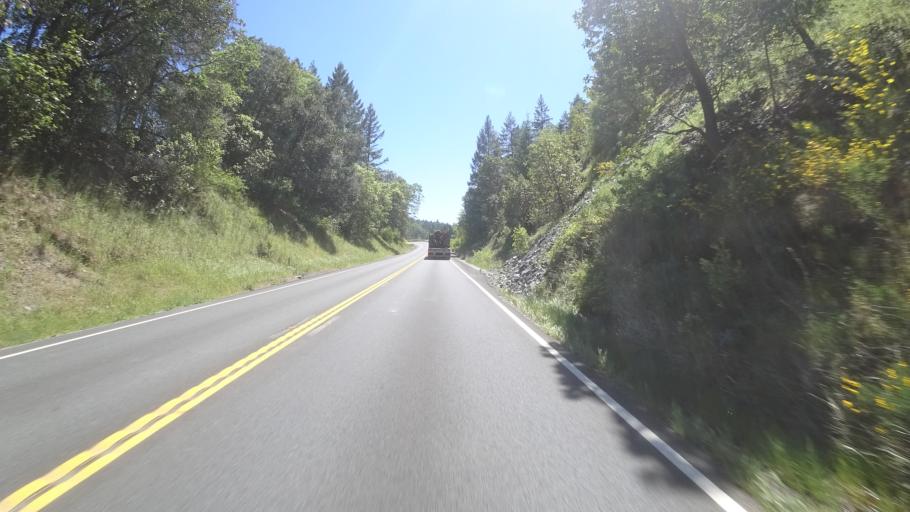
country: US
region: California
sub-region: Humboldt County
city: Willow Creek
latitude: 40.8900
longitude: -123.6063
